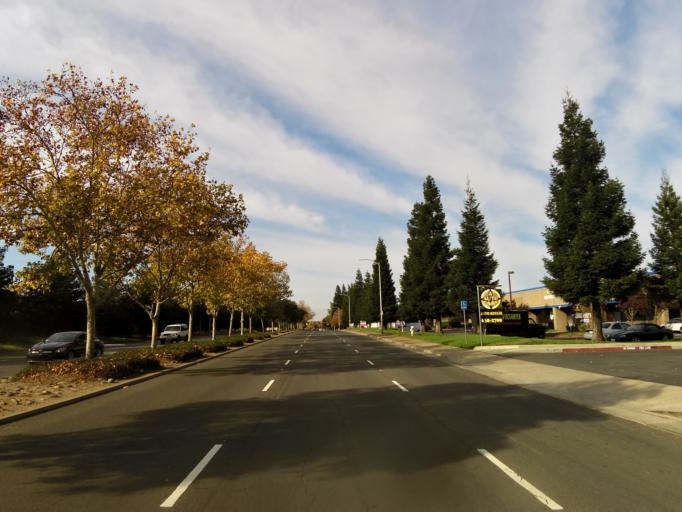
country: US
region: California
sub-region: Sacramento County
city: Rancho Cordova
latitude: 38.5743
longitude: -121.2578
